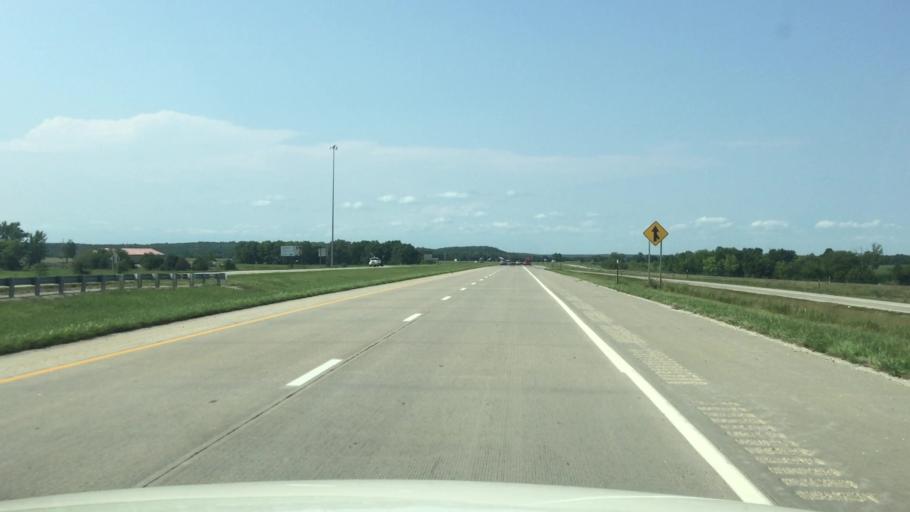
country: US
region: Kansas
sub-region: Linn County
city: Pleasanton
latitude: 38.1826
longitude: -94.7003
